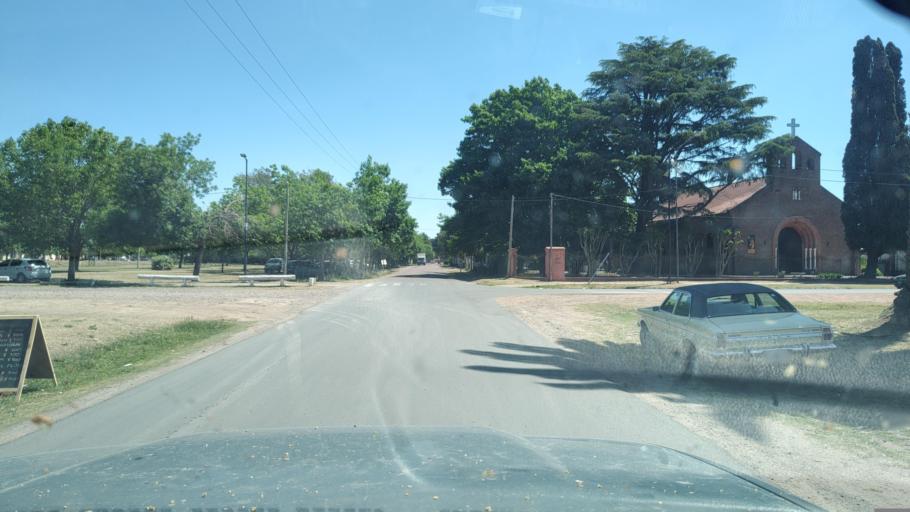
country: AR
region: Buenos Aires
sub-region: Partido de Lujan
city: Lujan
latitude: -34.6000
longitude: -59.1739
